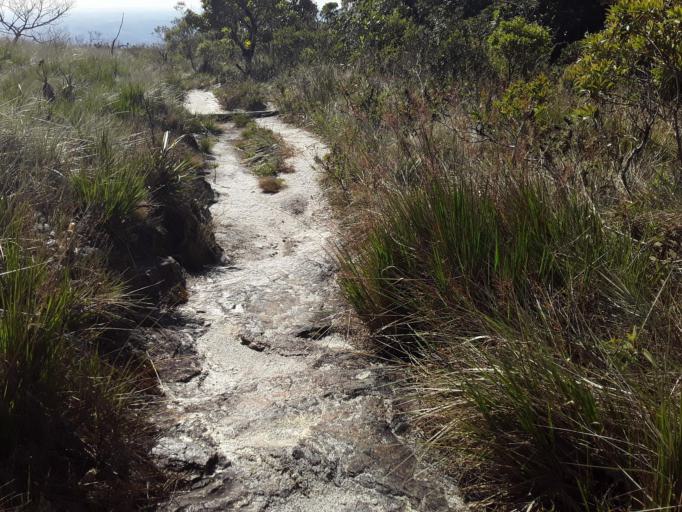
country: BR
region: Minas Gerais
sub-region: Lima Duarte
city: Lima Duarte
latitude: -21.6768
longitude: -43.8827
